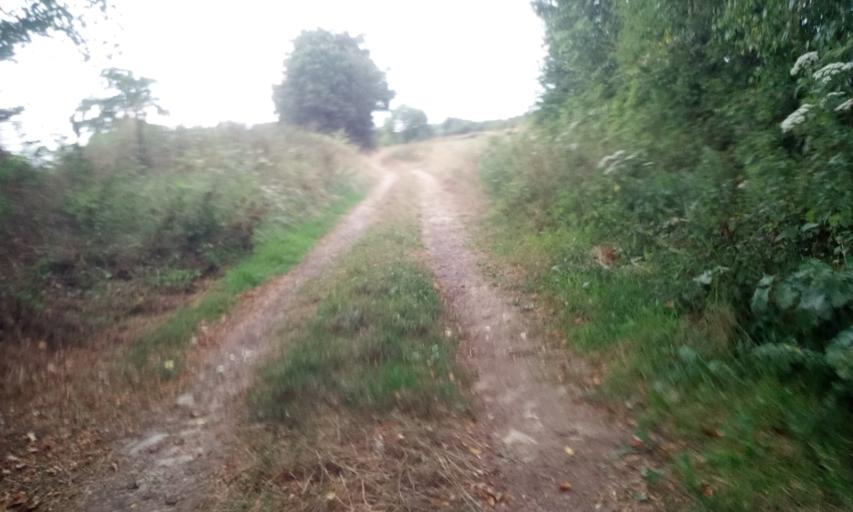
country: FR
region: Lower Normandy
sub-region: Departement du Calvados
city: Sannerville
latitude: 49.1897
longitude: -0.2182
